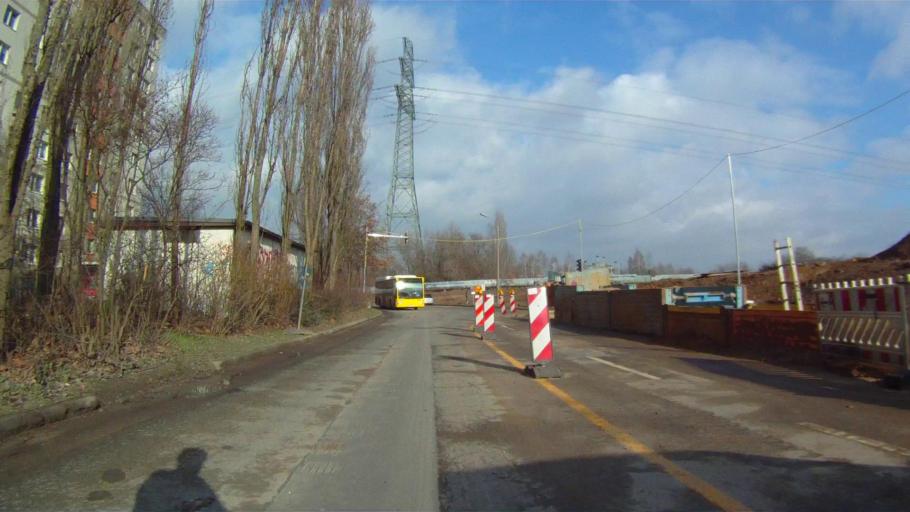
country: DE
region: Berlin
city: Biesdorf
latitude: 52.5125
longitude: 13.5330
